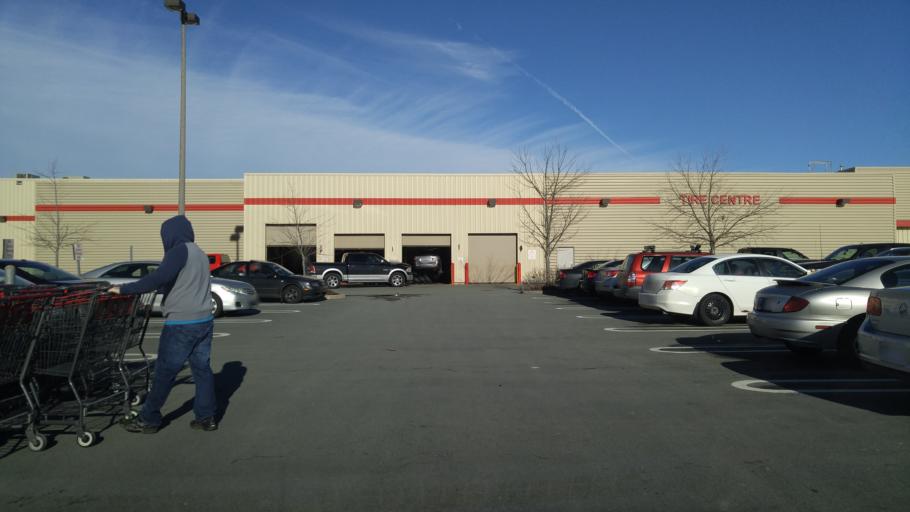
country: CA
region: Nova Scotia
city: Dartmouth
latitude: 44.7044
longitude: -63.5673
